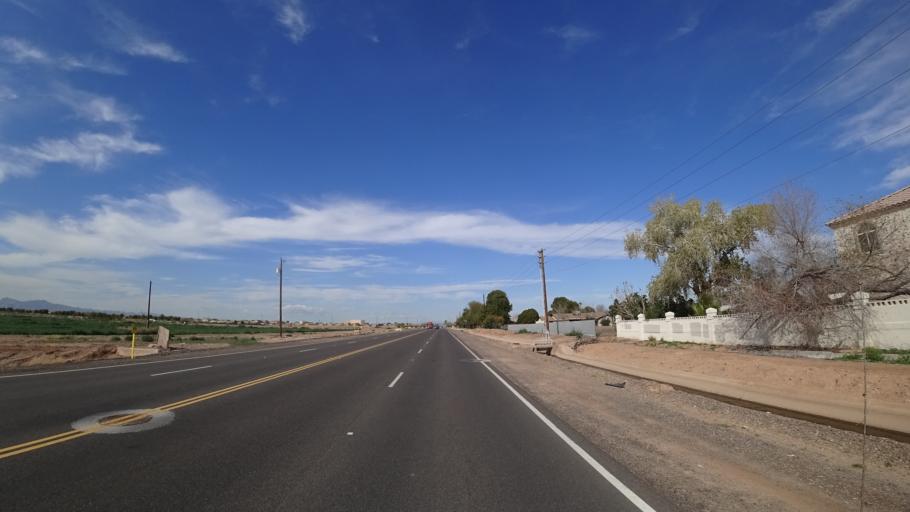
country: US
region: Arizona
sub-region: Maricopa County
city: Avondale
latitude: 33.4175
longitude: -112.3062
